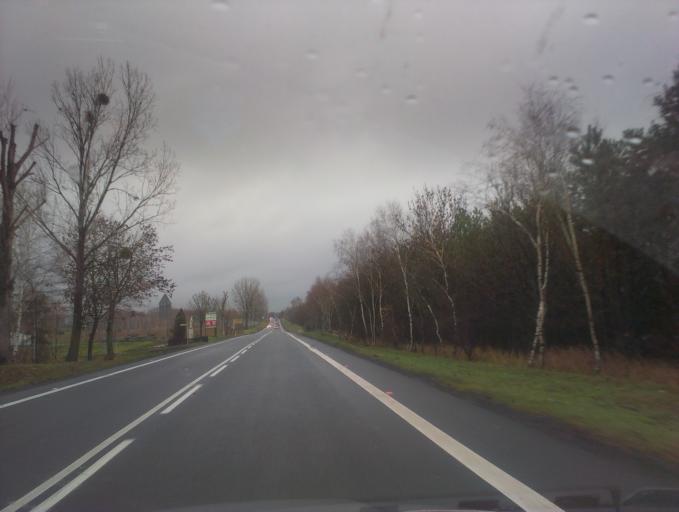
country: PL
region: Greater Poland Voivodeship
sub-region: Powiat poznanski
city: Zlotniki
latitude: 52.5388
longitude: 16.8373
